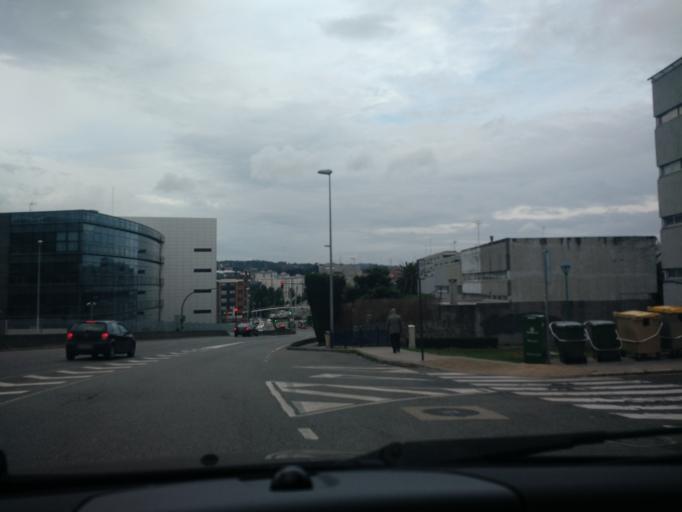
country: ES
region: Galicia
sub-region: Provincia da Coruna
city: A Coruna
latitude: 43.3430
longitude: -8.4005
